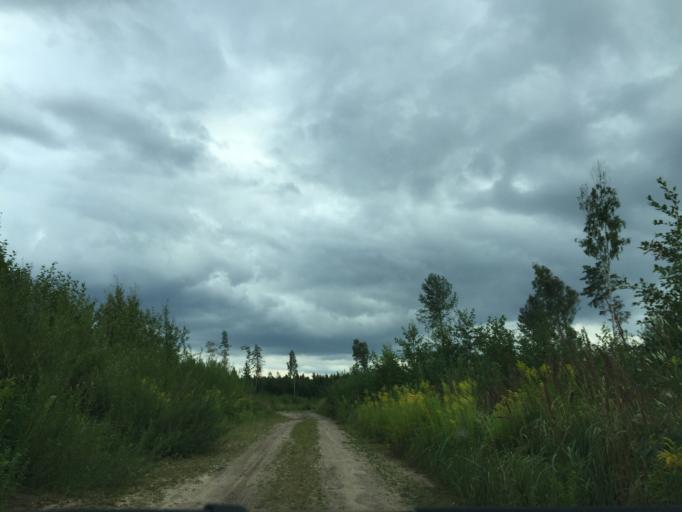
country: LV
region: Saulkrastu
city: Saulkrasti
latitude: 57.2344
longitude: 24.4642
